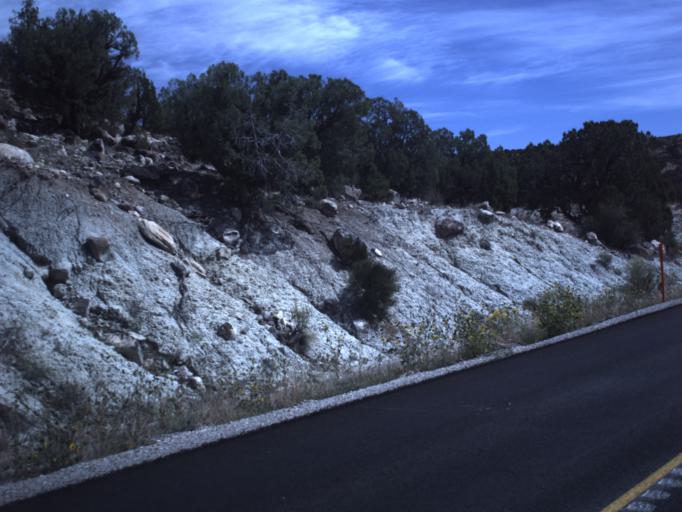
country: US
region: Utah
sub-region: San Juan County
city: Blanding
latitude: 37.5777
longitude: -109.5113
